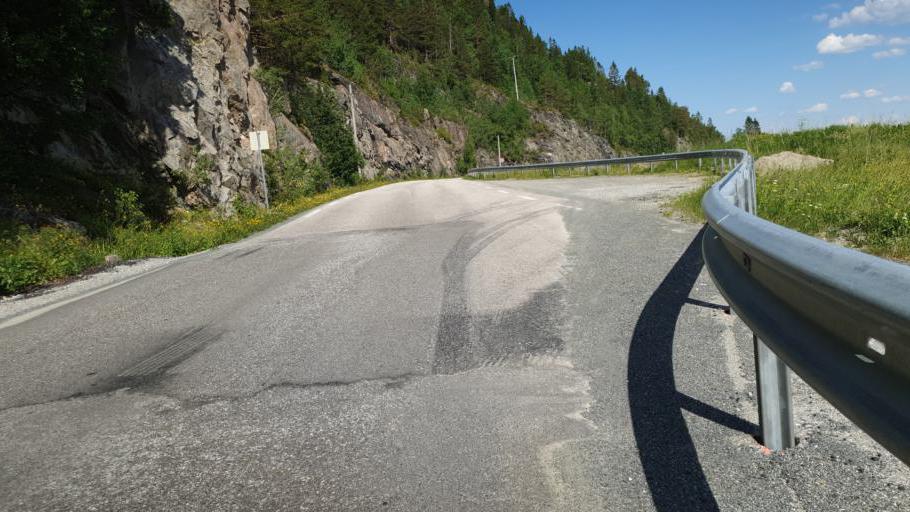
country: NO
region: Nord-Trondelag
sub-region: Leksvik
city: Leksvik
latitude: 63.6022
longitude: 10.4714
